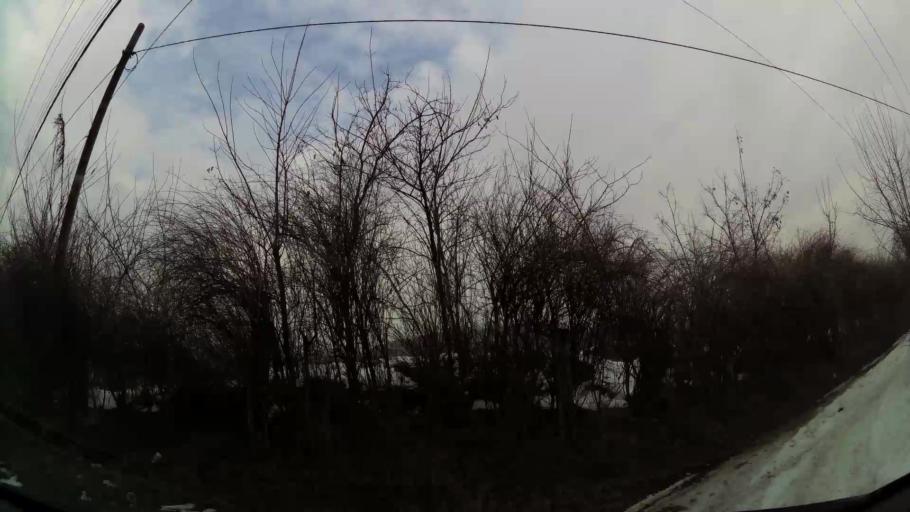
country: MK
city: Kondovo
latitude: 42.0321
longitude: 21.3351
